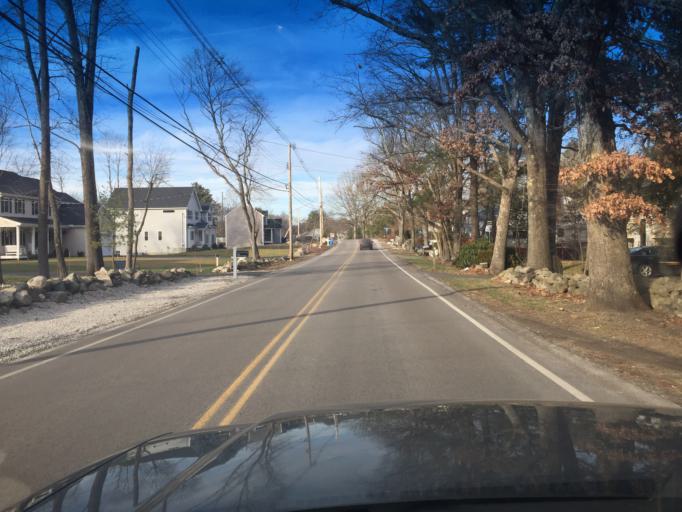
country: US
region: Massachusetts
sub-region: Middlesex County
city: Holliston
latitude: 42.1805
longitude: -71.4115
